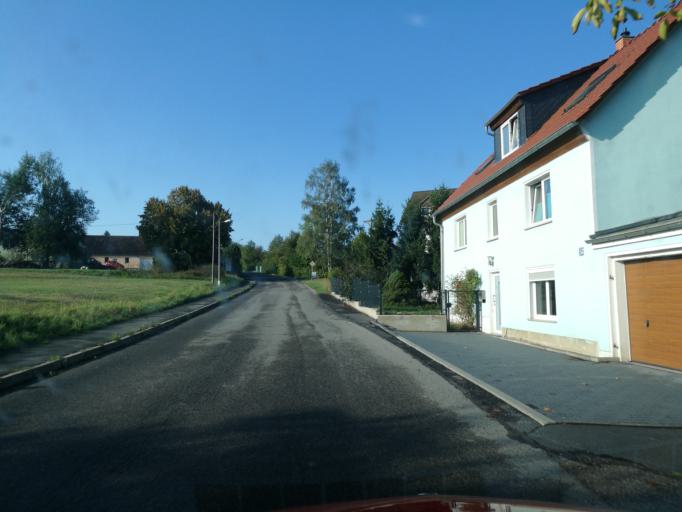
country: DE
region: Saxony
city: Klipphausen
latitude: 51.1070
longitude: 13.4839
